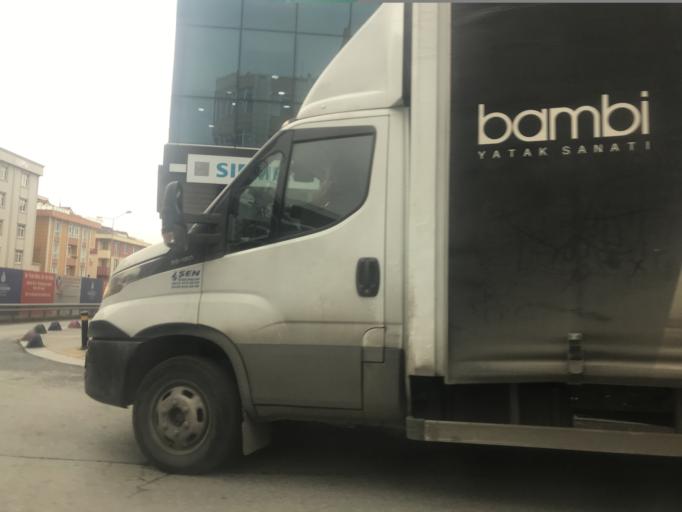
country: TR
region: Istanbul
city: Bagcilar
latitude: 41.0238
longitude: 28.8380
